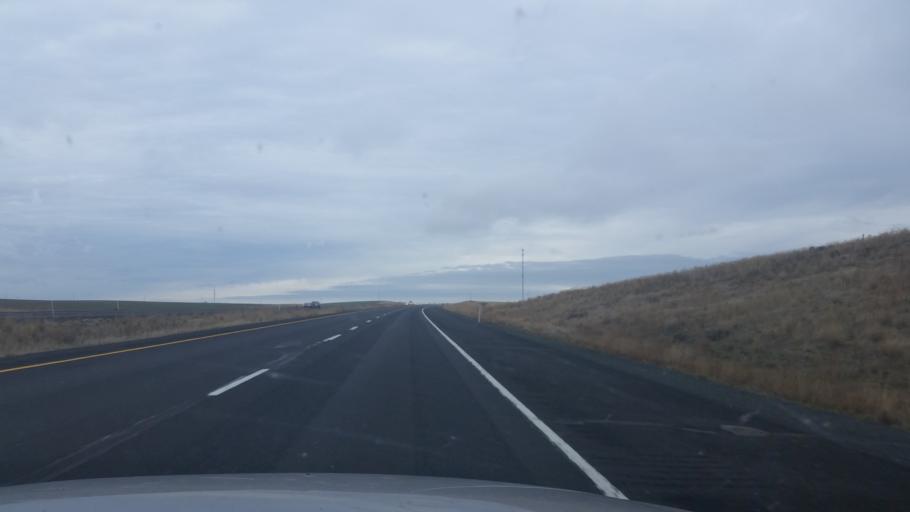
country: US
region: Washington
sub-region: Adams County
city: Ritzville
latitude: 47.1112
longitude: -118.4366
